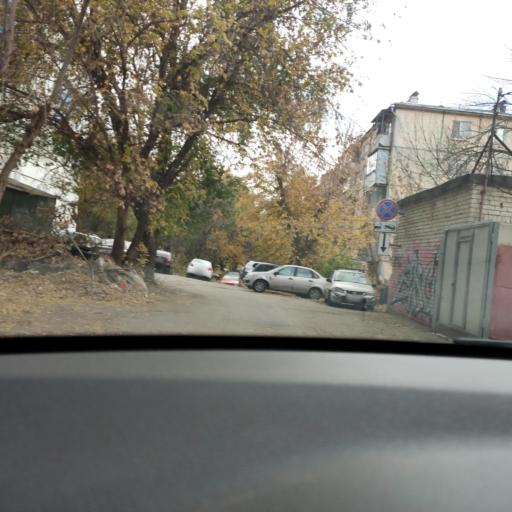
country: RU
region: Samara
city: Samara
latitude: 53.1976
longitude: 50.1649
